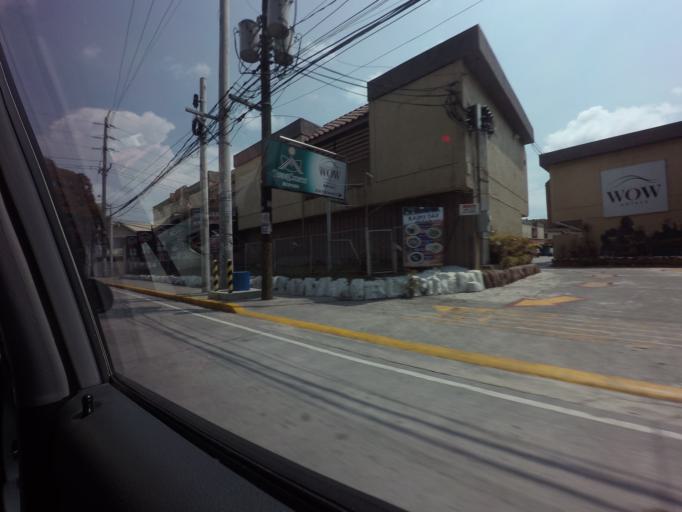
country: PH
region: Metro Manila
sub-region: San Juan
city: San Juan
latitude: 14.5978
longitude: 121.0166
